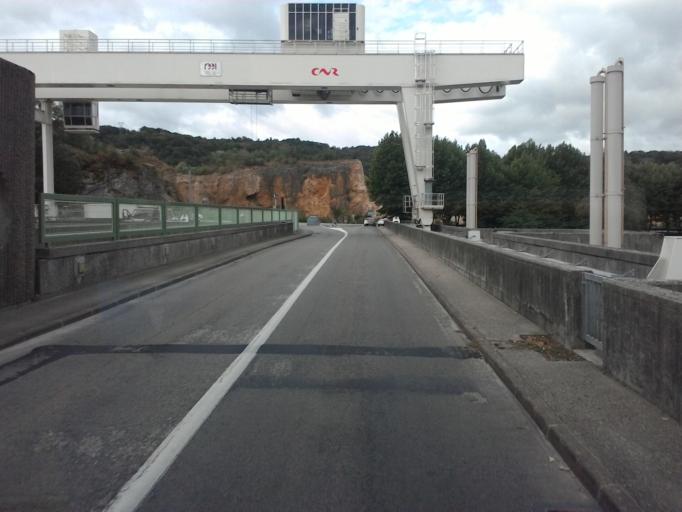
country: FR
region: Rhone-Alpes
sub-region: Departement de l'Ain
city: Sault-Brenaz
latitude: 45.8534
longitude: 5.4062
